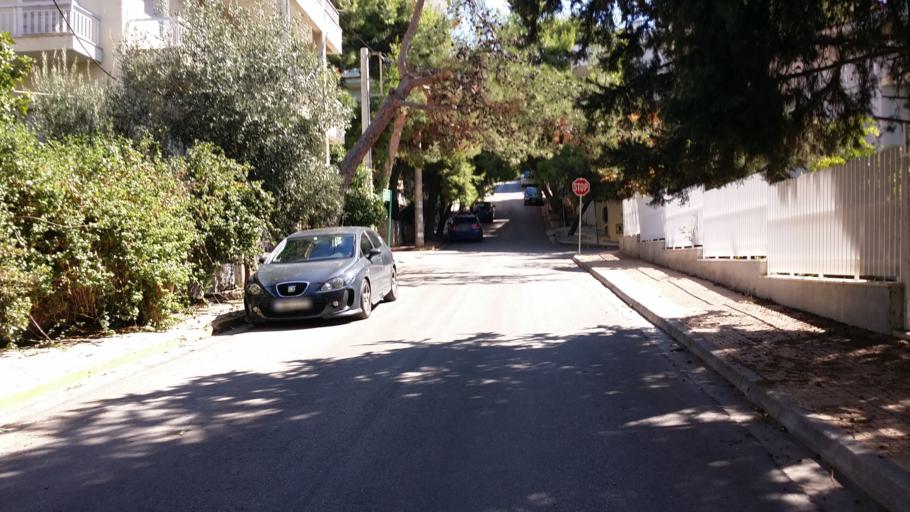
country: GR
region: Attica
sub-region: Nomarchia Athinas
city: Irakleio
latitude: 38.0463
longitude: 23.7615
